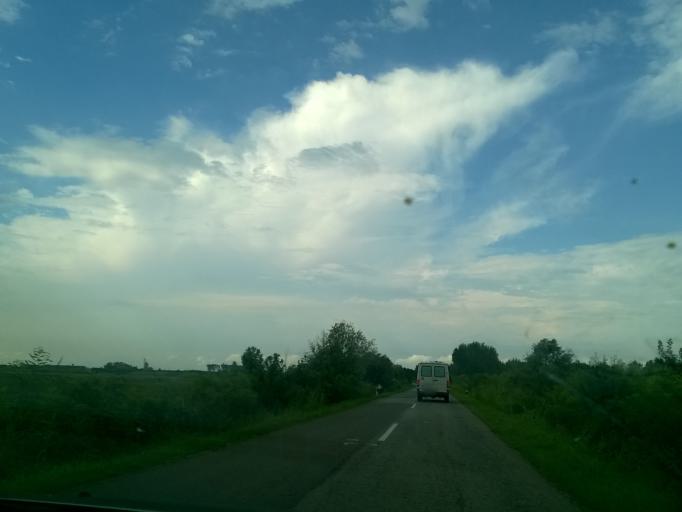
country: RS
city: Tomasevac
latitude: 45.2545
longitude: 20.6110
